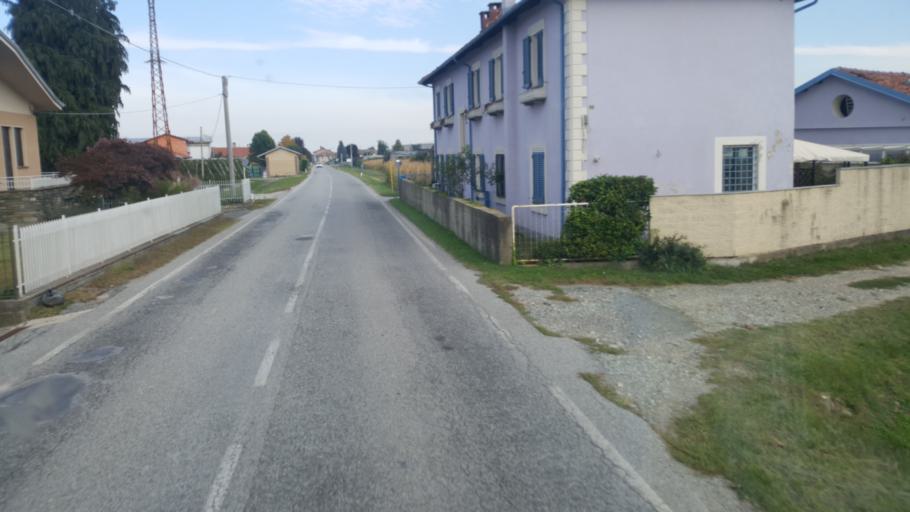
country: IT
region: Piedmont
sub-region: Provincia di Cuneo
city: Verzuolo
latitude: 44.5975
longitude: 7.5035
